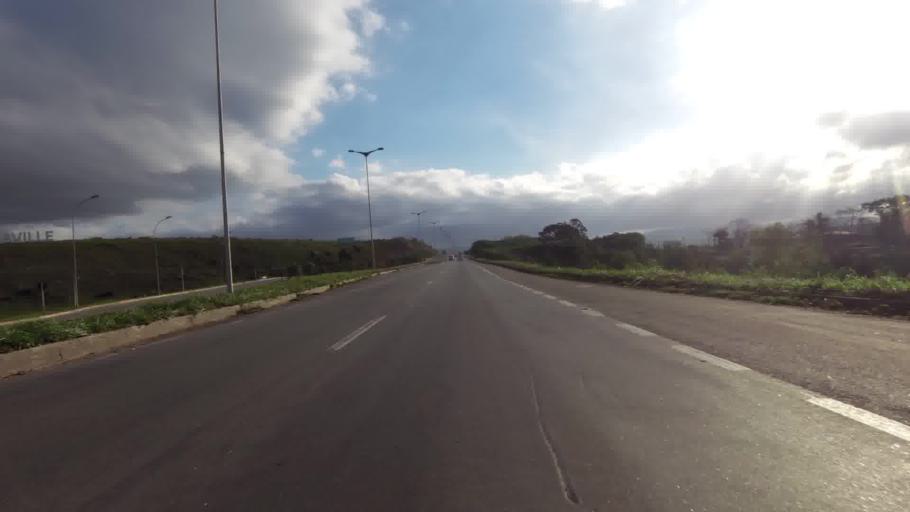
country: BR
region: Espirito Santo
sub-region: Serra
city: Serra
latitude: -20.2167
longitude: -40.3278
